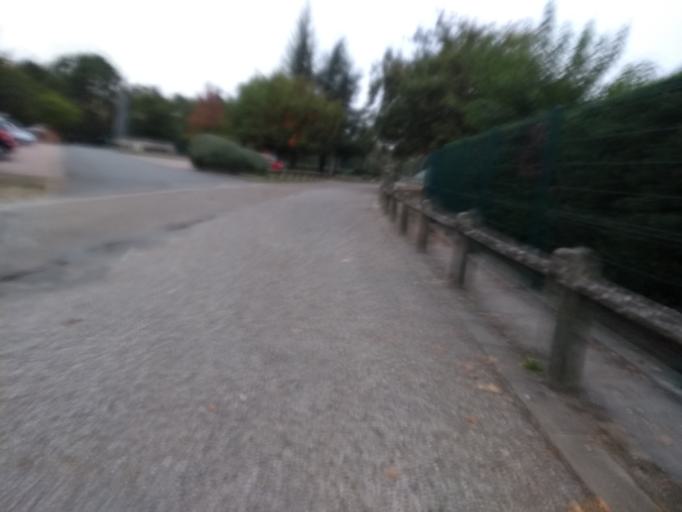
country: FR
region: Aquitaine
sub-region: Departement de la Gironde
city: Talence
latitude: 44.7922
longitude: -0.5981
